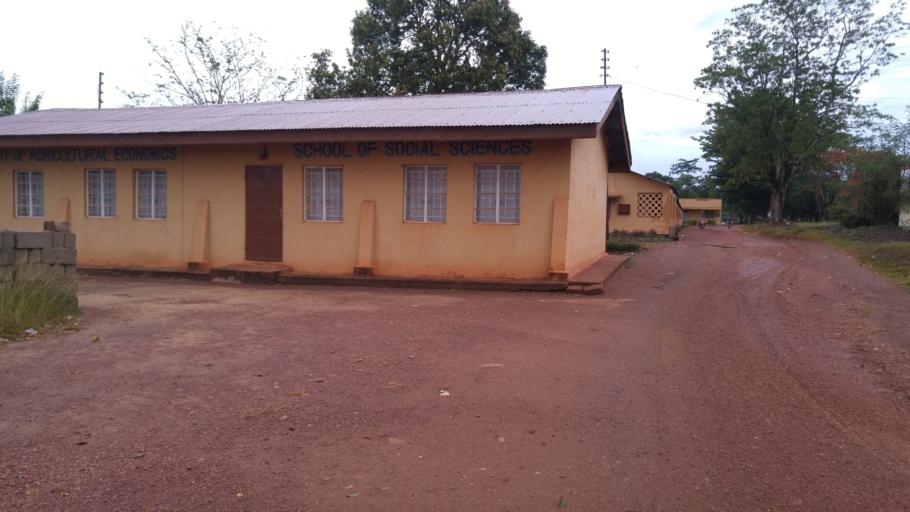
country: SL
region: Southern Province
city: Largo
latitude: 8.1134
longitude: -12.0711
